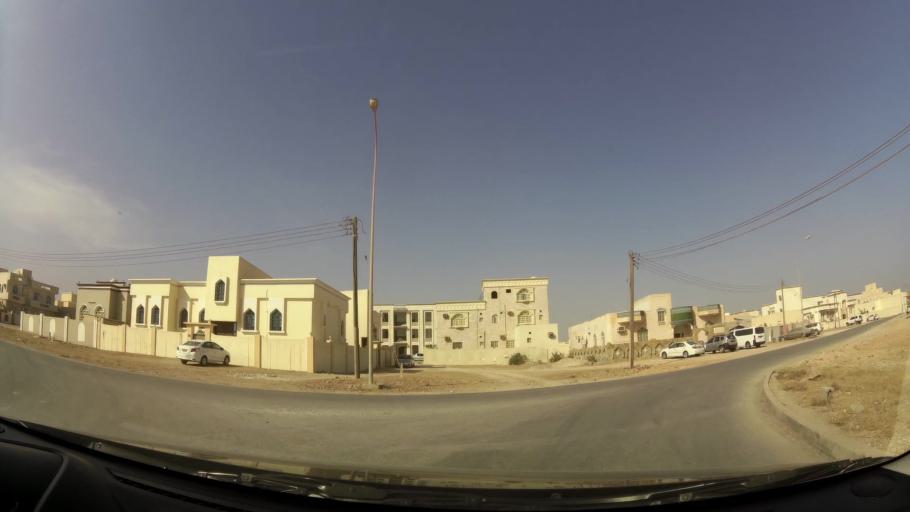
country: OM
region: Zufar
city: Salalah
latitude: 17.0119
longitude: 54.0086
